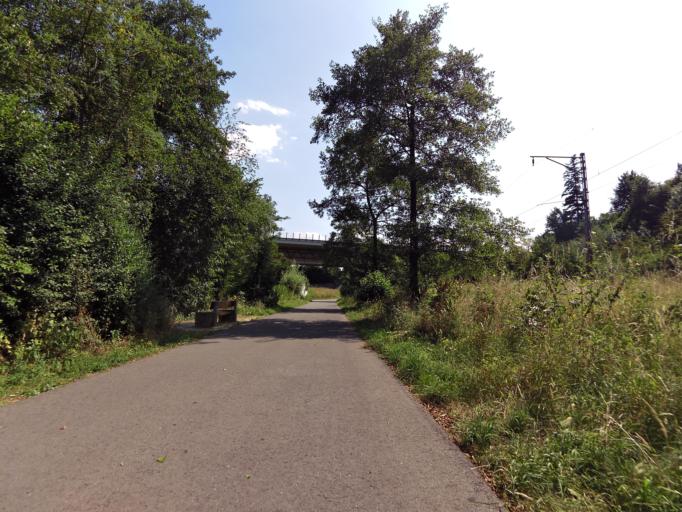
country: CH
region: Aargau
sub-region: Bezirk Baden
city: Baden
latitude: 47.4598
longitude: 8.2864
